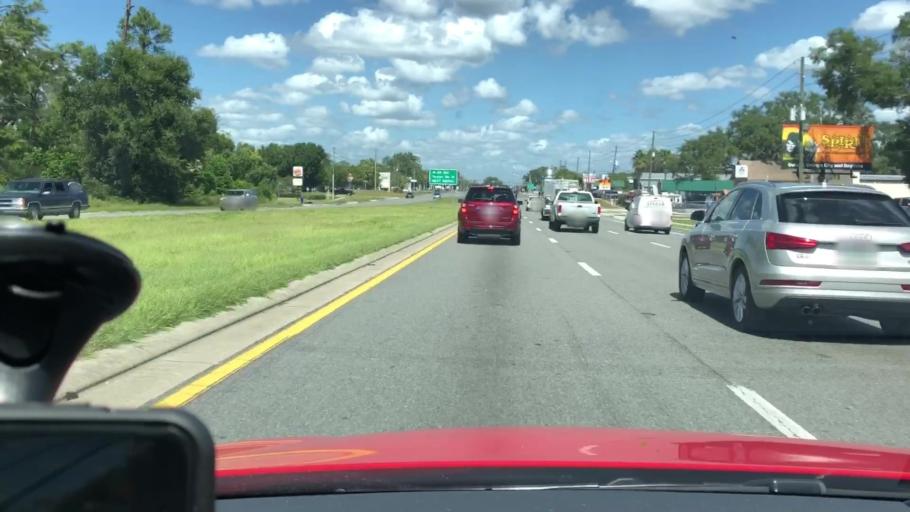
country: US
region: Florida
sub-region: Volusia County
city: De Land Southwest
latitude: 28.9943
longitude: -81.3024
